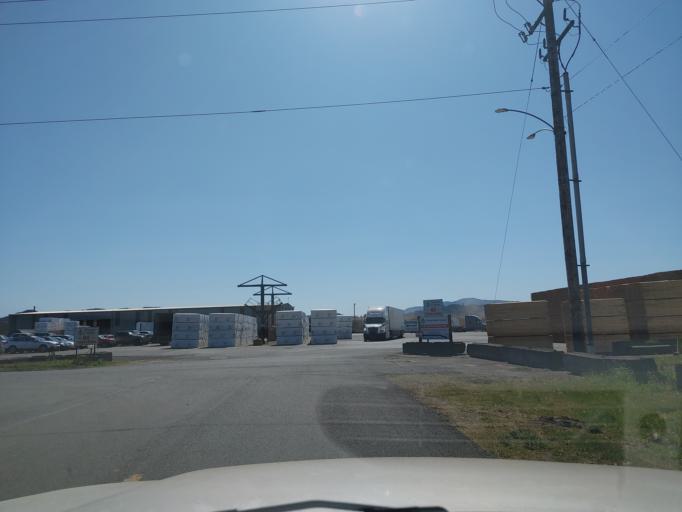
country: US
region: Oregon
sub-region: Tillamook County
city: Tillamook
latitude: 45.4190
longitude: -123.8055
